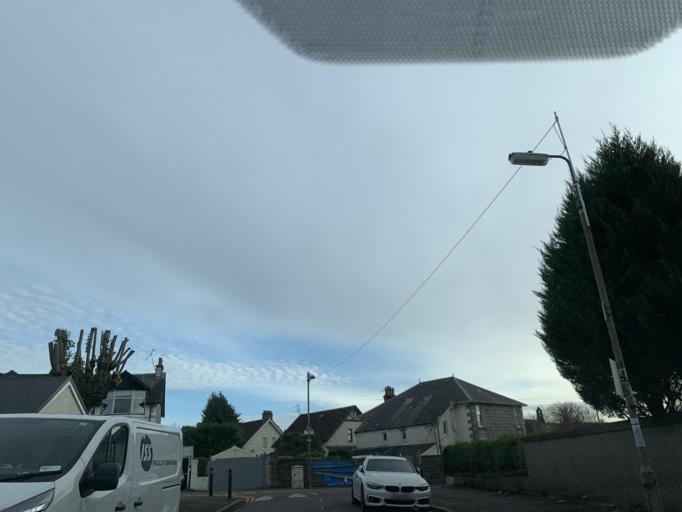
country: GB
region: Scotland
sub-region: Renfrewshire
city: Renfrew
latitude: 55.8465
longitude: -4.3569
